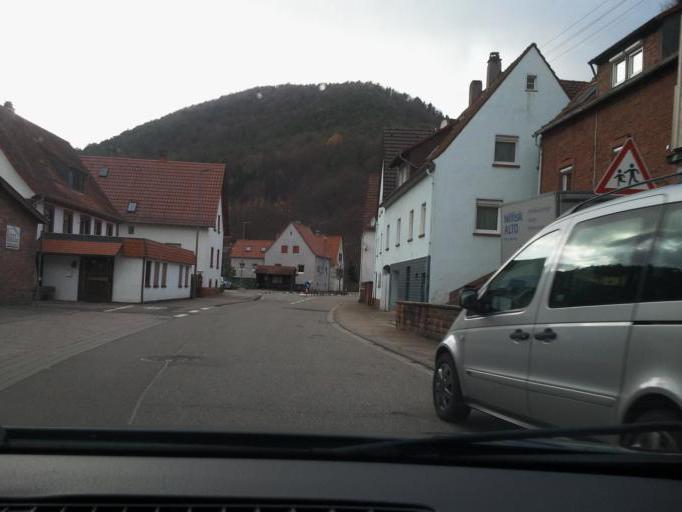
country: DE
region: Rheinland-Pfalz
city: Rinnthal
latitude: 49.2187
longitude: 7.9226
